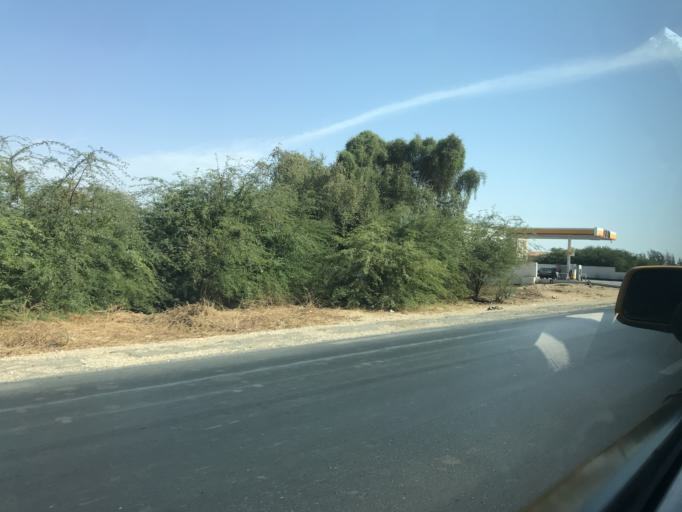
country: SN
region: Saint-Louis
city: Saint-Louis
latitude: 16.0521
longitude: -16.4298
